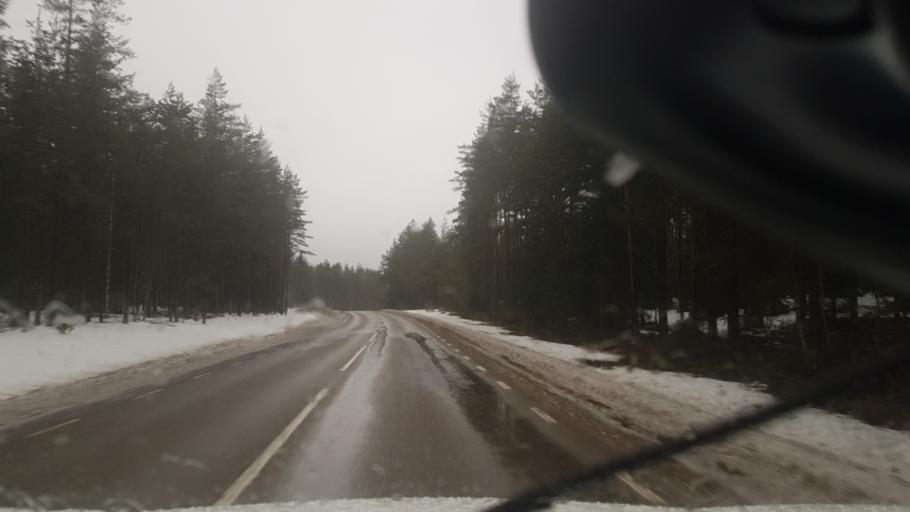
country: SE
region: Vaermland
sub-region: Arjangs Kommun
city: Arjaeng
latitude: 59.5558
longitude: 12.1619
